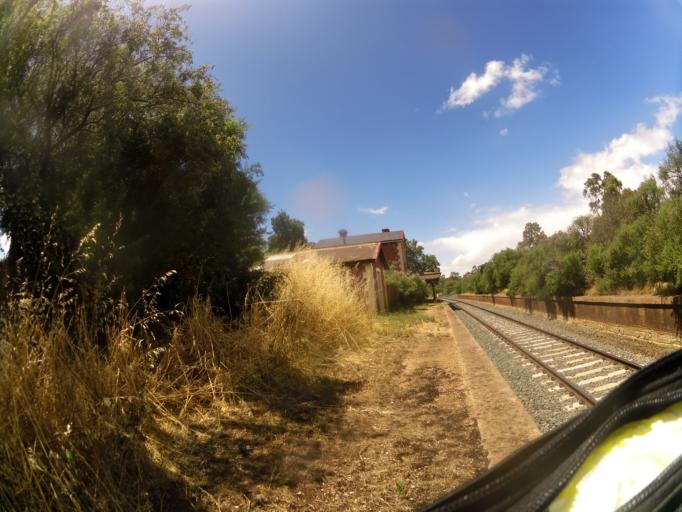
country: AU
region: Victoria
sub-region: Mount Alexander
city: Castlemaine
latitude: -37.0044
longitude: 144.2528
